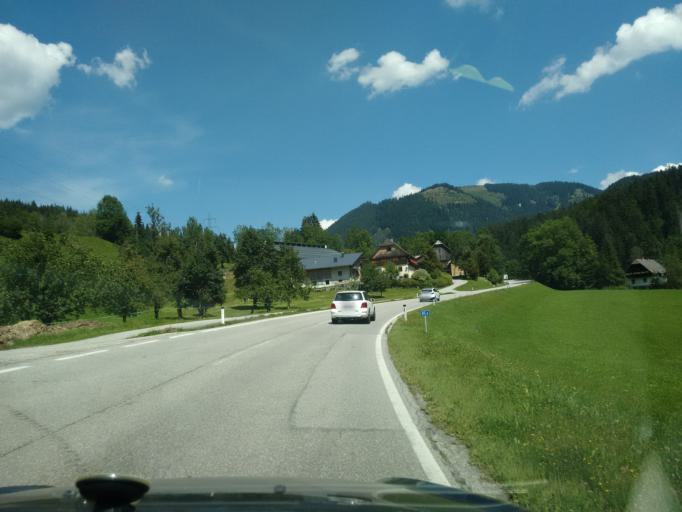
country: AT
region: Styria
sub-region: Politischer Bezirk Liezen
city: Liezen
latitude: 47.5821
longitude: 14.2684
